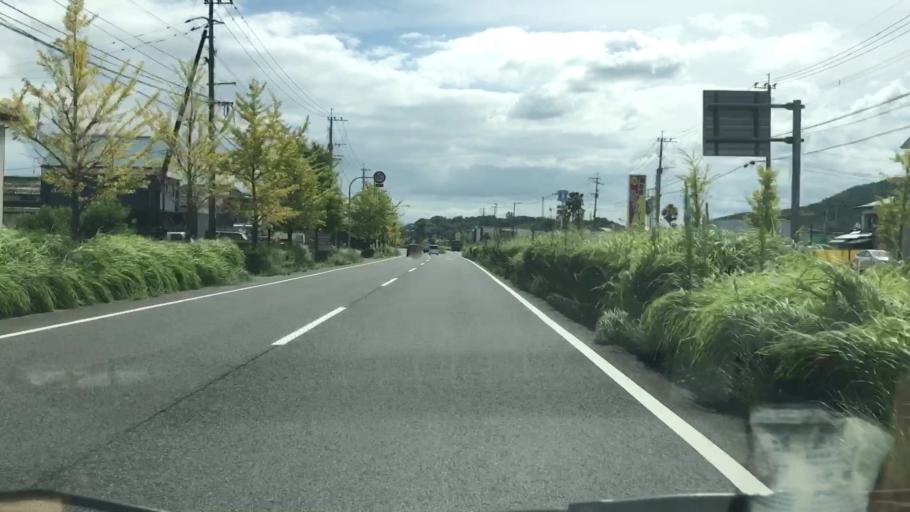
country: JP
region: Saga Prefecture
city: Saga-shi
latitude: 33.2398
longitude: 130.1841
